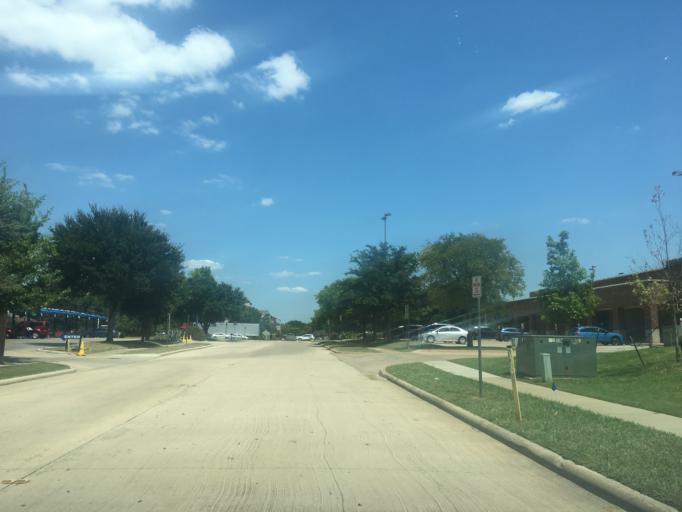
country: US
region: Texas
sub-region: Denton County
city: Lewisville
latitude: 33.0162
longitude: -96.9945
